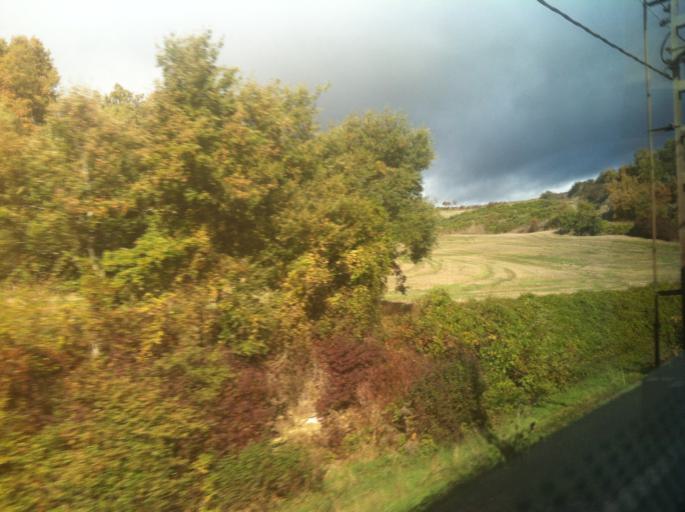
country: ES
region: Basque Country
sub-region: Provincia de Alava
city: Arminon
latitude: 42.7376
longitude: -2.8744
